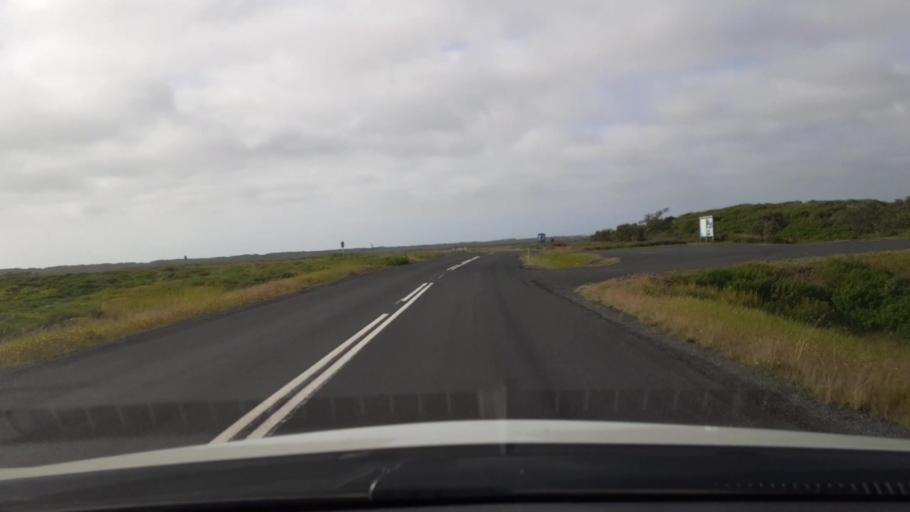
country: IS
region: South
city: THorlakshoefn
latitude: 63.8927
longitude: -21.3640
